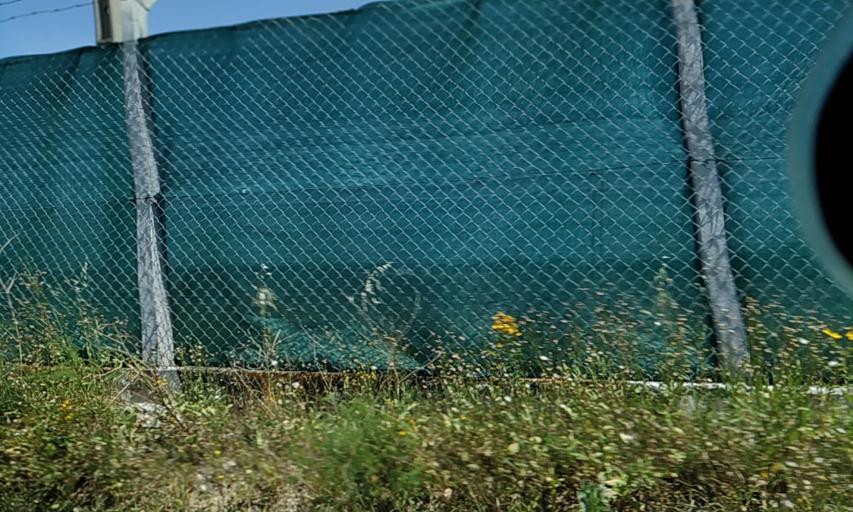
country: PT
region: Santarem
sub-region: Benavente
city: Poceirao
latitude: 38.6672
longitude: -8.7368
